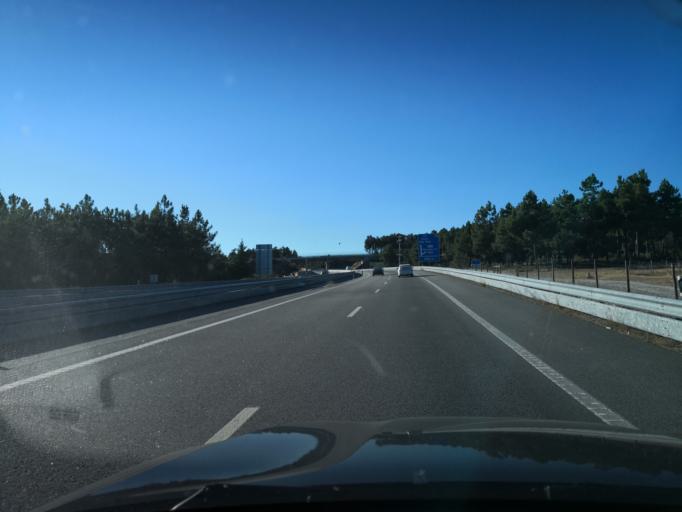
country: PT
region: Vila Real
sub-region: Murca
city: Murca
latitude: 41.3784
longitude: -7.4969
